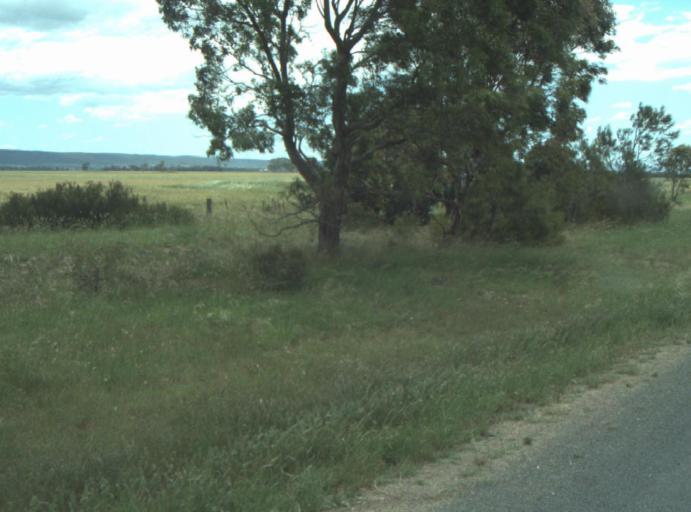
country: AU
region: Victoria
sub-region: Greater Geelong
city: Lara
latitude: -37.8801
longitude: 144.3794
